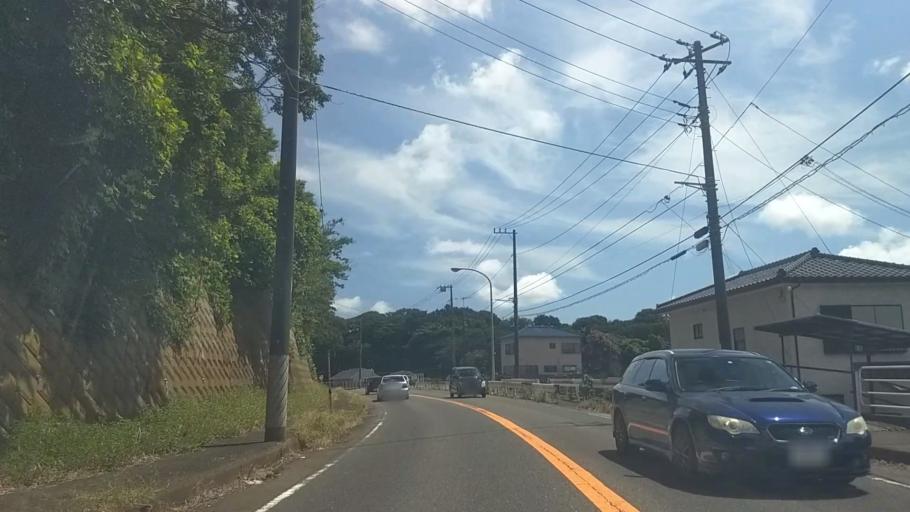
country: JP
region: Kanagawa
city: Miura
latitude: 35.2096
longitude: 139.6440
